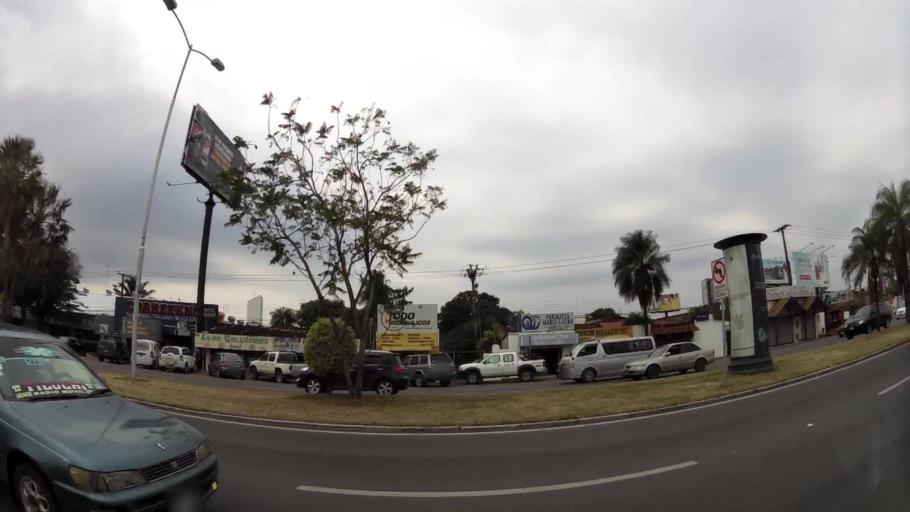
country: BO
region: Santa Cruz
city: Santa Cruz de la Sierra
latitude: -17.7697
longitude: -63.1827
